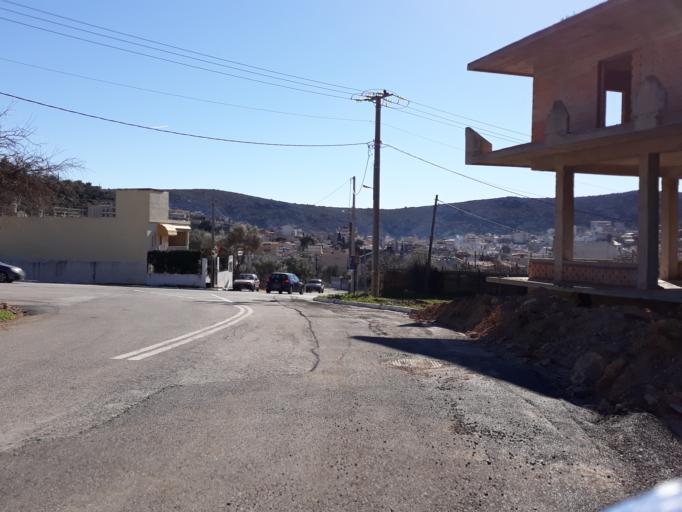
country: GR
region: Attica
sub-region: Nomarchia Dytikis Attikis
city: Fyli
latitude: 38.1093
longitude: 23.6704
